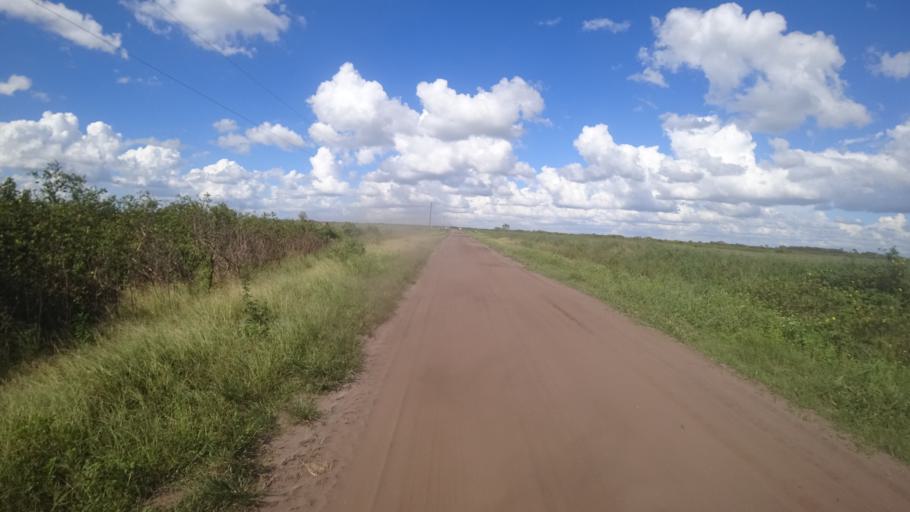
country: US
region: Florida
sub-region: DeSoto County
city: Arcadia
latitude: 27.3321
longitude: -82.0969
